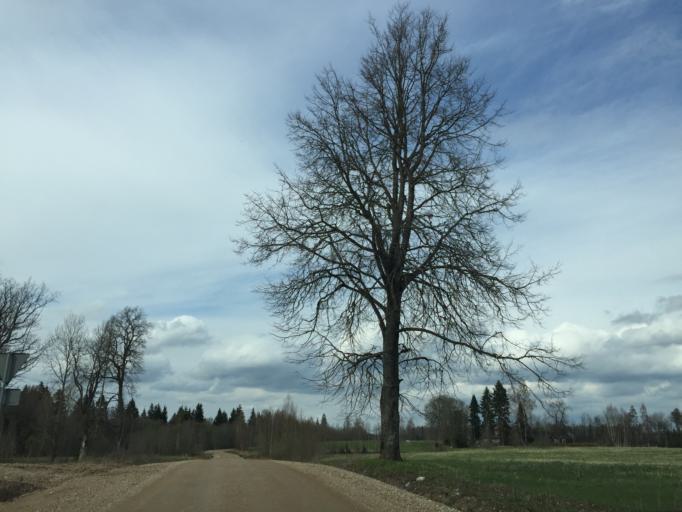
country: LV
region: Ligatne
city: Ligatne
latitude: 57.1904
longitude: 25.0629
